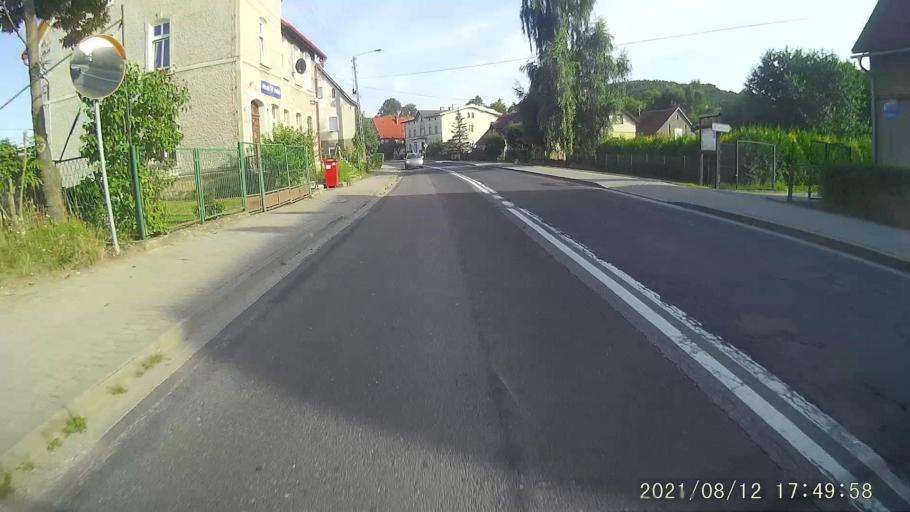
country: PL
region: Lower Silesian Voivodeship
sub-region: Powiat klodzki
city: Klodzko
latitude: 50.3633
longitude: 16.7133
